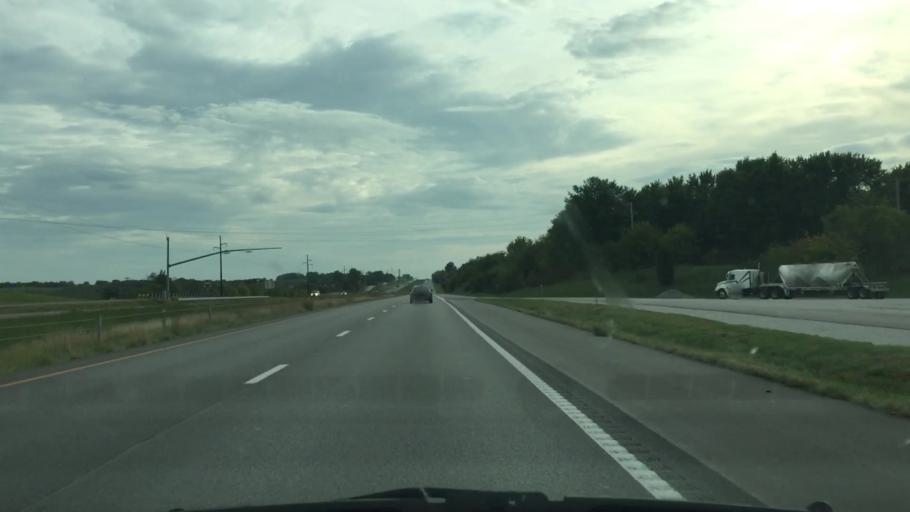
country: US
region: Missouri
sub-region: Clay County
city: Kearney
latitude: 39.3172
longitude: -94.3998
